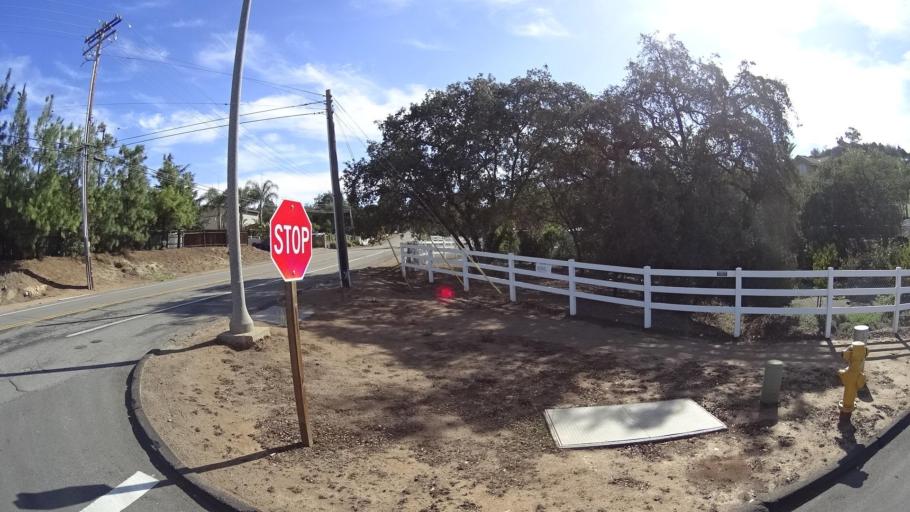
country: US
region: California
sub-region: San Diego County
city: Alpine
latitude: 32.8157
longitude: -116.7718
